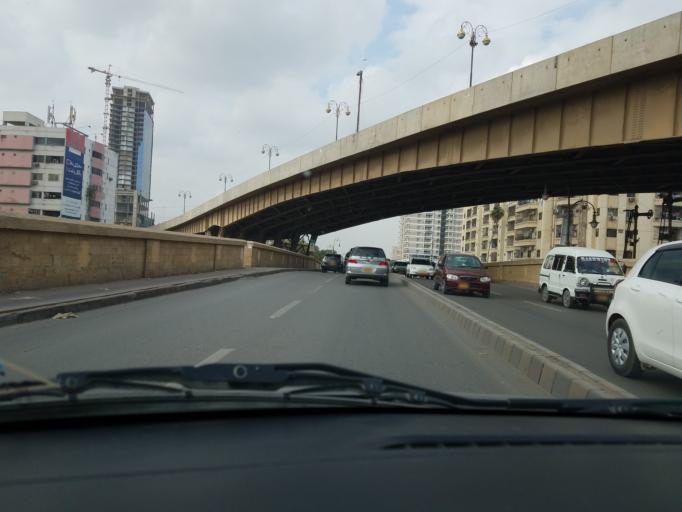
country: PK
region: Sindh
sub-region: Karachi District
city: Karachi
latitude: 24.8404
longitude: 67.0327
